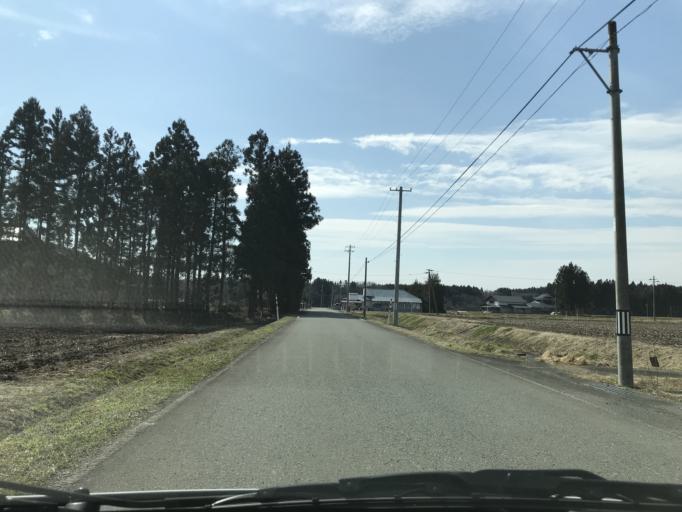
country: JP
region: Iwate
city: Mizusawa
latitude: 39.1236
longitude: 141.0432
